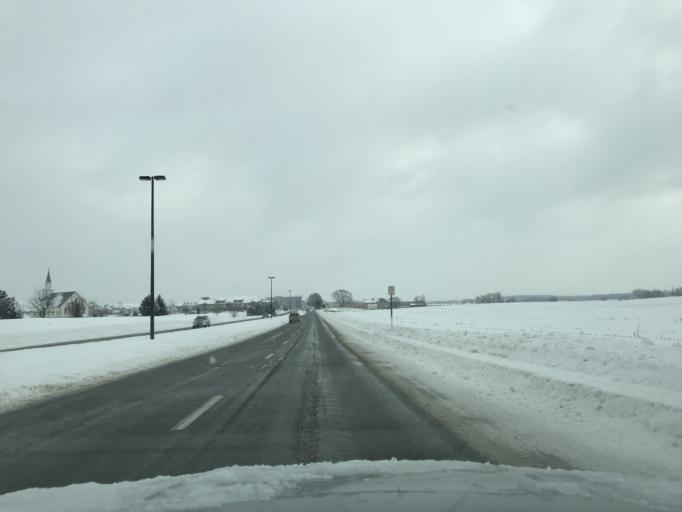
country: US
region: Wisconsin
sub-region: Dane County
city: Sun Prairie
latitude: 43.1649
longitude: -89.2824
